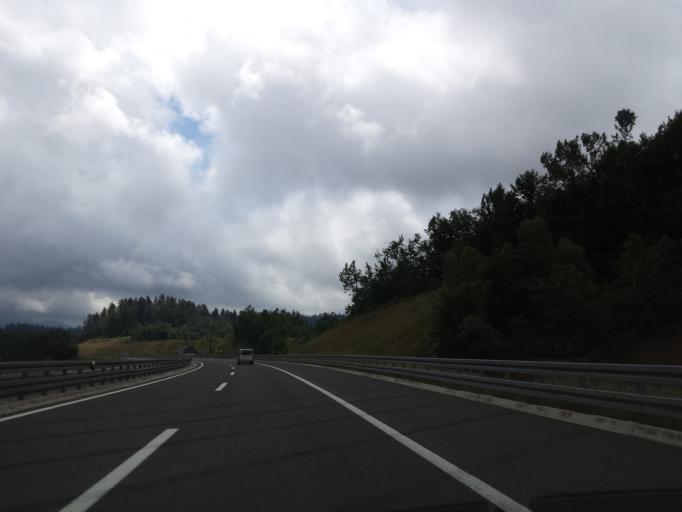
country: HR
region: Primorsko-Goranska
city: Hreljin
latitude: 45.3211
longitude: 14.6646
